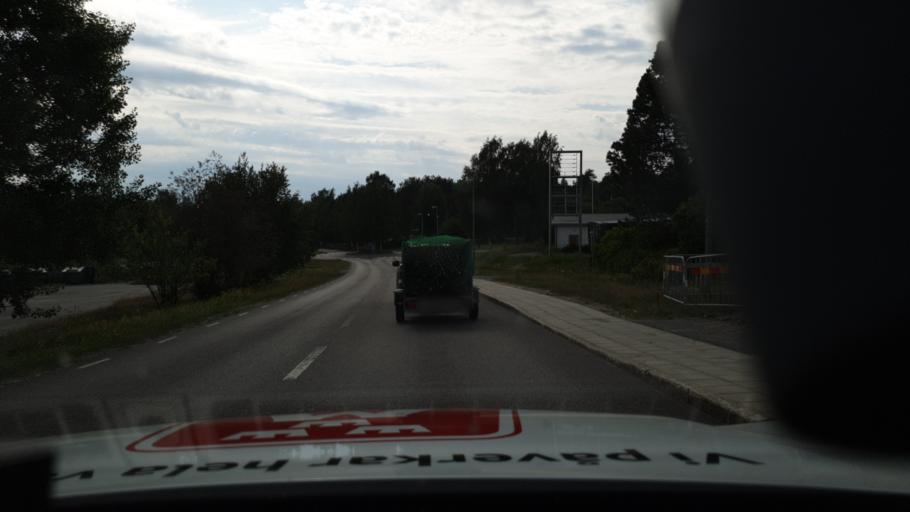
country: SE
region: Norrbotten
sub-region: Lulea Kommun
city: Ranea
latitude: 65.8623
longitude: 22.3001
